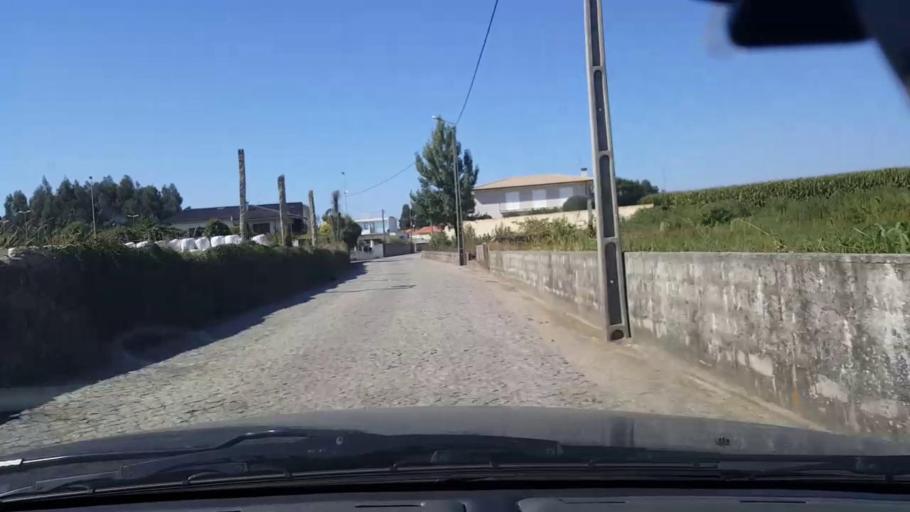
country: PT
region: Porto
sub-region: Matosinhos
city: Lavra
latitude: 41.2924
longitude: -8.6974
